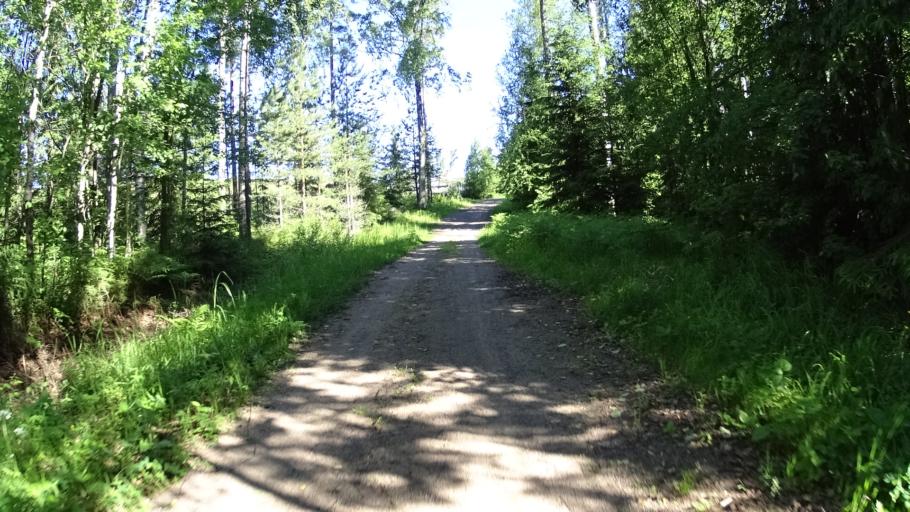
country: FI
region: Uusimaa
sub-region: Helsinki
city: Kilo
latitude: 60.3060
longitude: 24.8117
